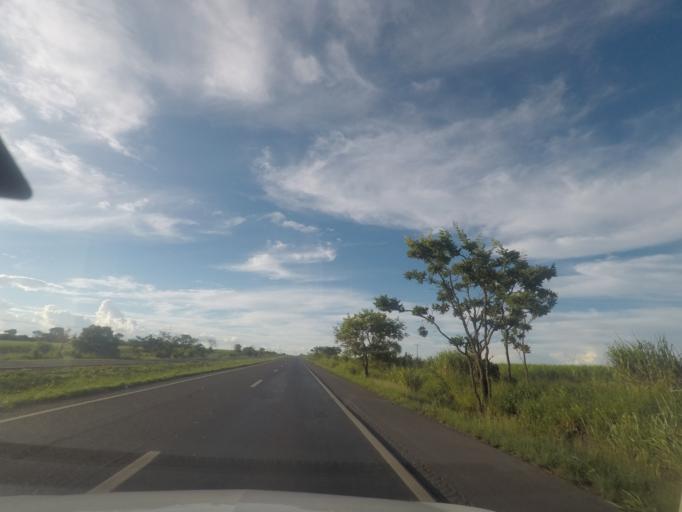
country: BR
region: Goias
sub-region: Itumbiara
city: Itumbiara
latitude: -18.2214
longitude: -49.2677
